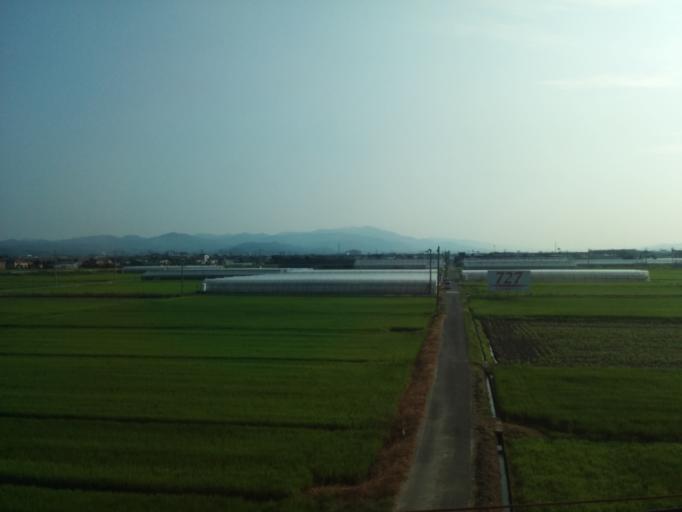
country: JP
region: Aichi
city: Kozakai-cho
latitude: 34.7989
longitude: 137.3267
